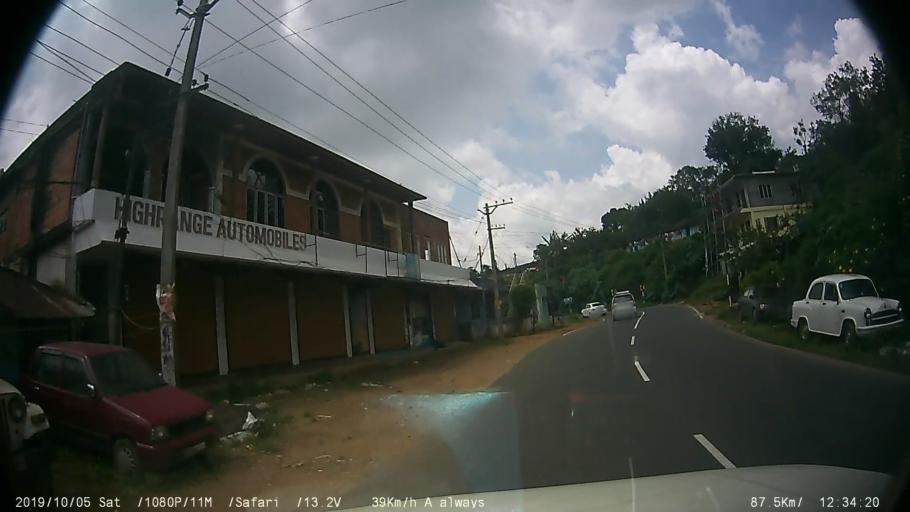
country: IN
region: Tamil Nadu
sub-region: Theni
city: Gudalur
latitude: 9.5778
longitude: 77.0171
